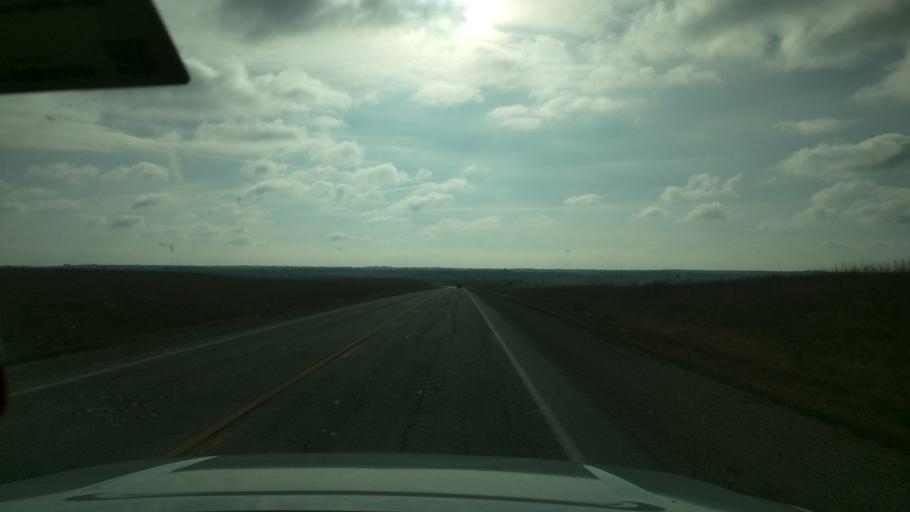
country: US
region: Kansas
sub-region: Chautauqua County
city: Sedan
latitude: 37.0924
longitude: -96.2275
